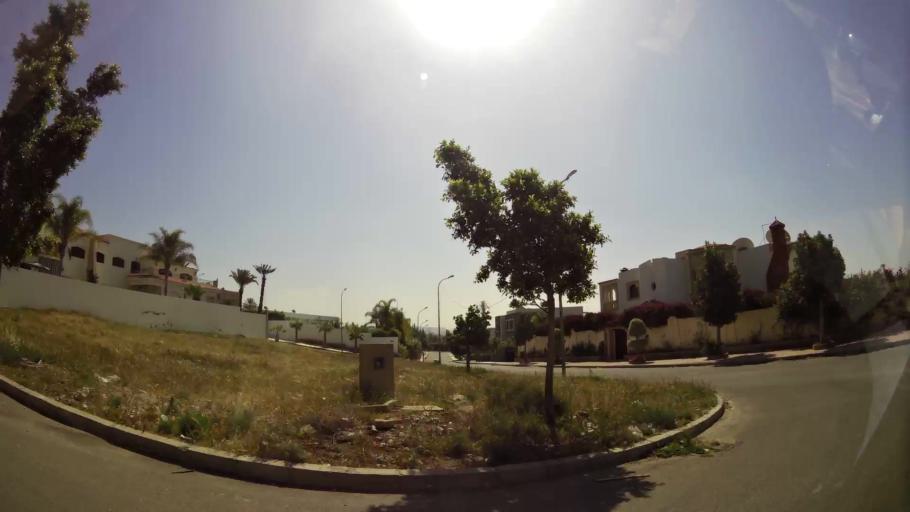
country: MA
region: Souss-Massa-Draa
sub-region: Agadir-Ida-ou-Tnan
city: Agadir
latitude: 30.4417
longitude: -9.5931
